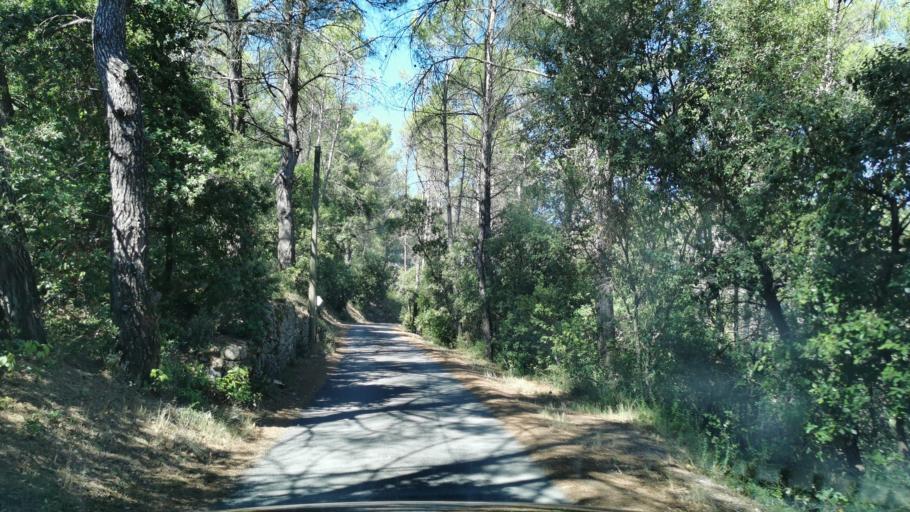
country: FR
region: Languedoc-Roussillon
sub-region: Departement de l'Aude
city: Conques-sur-Orbiel
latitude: 43.2447
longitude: 2.4116
